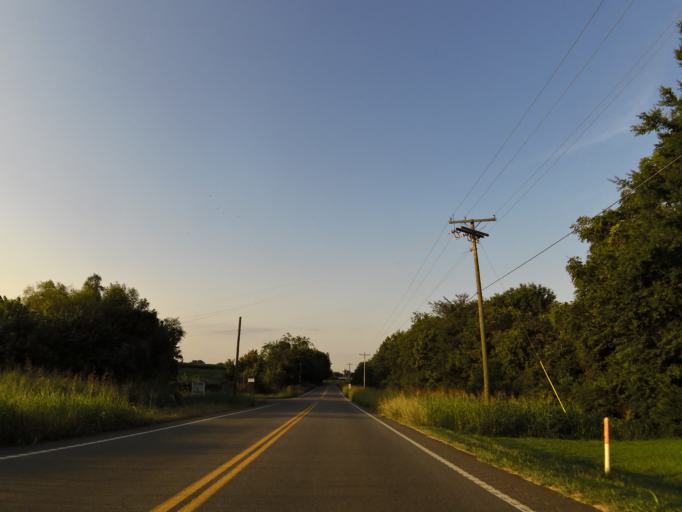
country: US
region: Tennessee
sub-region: Monroe County
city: Sweetwater
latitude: 35.5642
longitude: -84.5050
